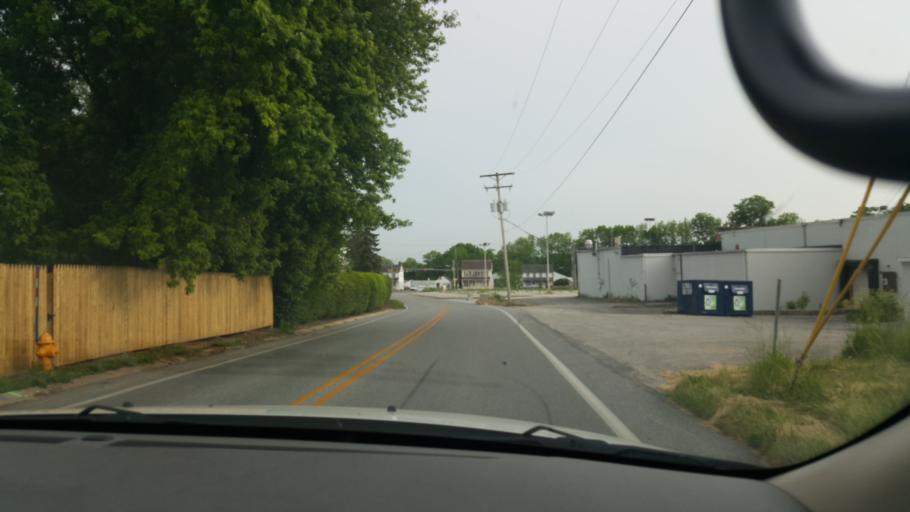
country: US
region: Pennsylvania
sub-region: York County
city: Weigelstown
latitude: 39.9840
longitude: -76.8166
